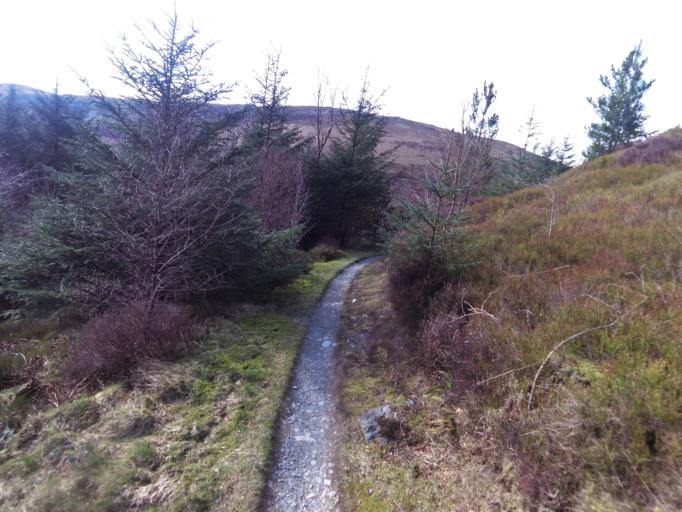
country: GB
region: Wales
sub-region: County of Ceredigion
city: Bow Street
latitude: 52.4269
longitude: -3.8871
